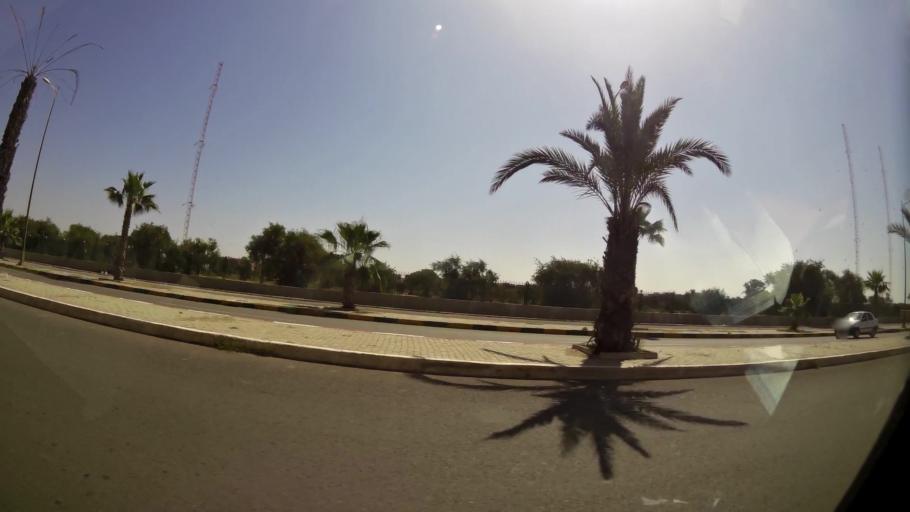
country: MA
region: Souss-Massa-Draa
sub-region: Inezgane-Ait Mellou
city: Inezgane
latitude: 30.3287
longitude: -9.5038
